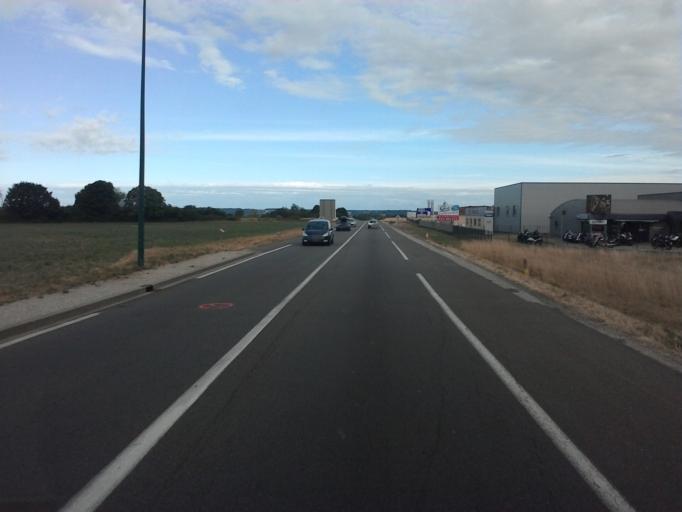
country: FR
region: Rhone-Alpes
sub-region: Departement de l'Ain
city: Saint-Denis-en-Bugey
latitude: 45.9414
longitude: 5.3310
